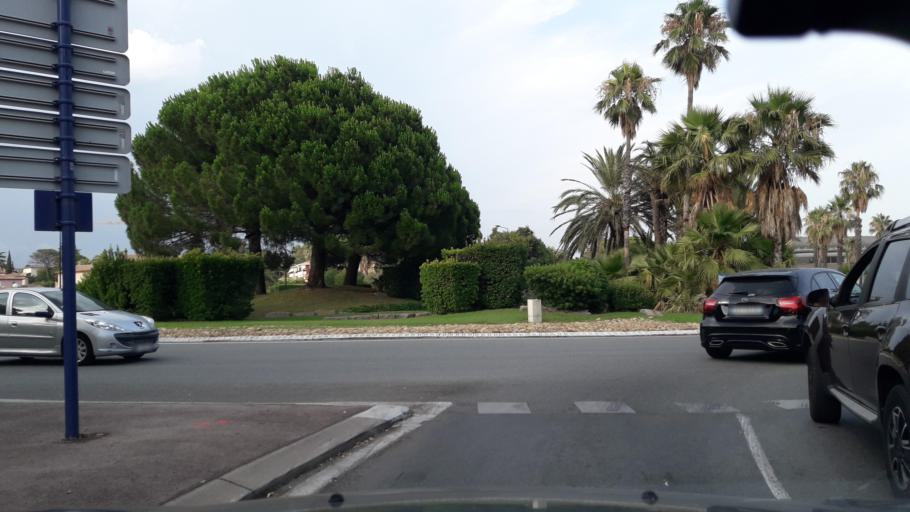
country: FR
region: Provence-Alpes-Cote d'Azur
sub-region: Departement du Var
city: Frejus
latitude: 43.4374
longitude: 6.7549
